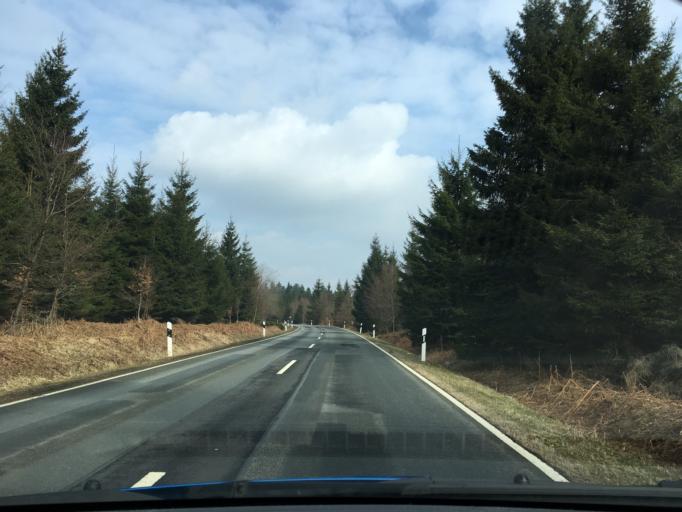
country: DE
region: Lower Saxony
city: Heinade
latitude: 51.7679
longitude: 9.5737
